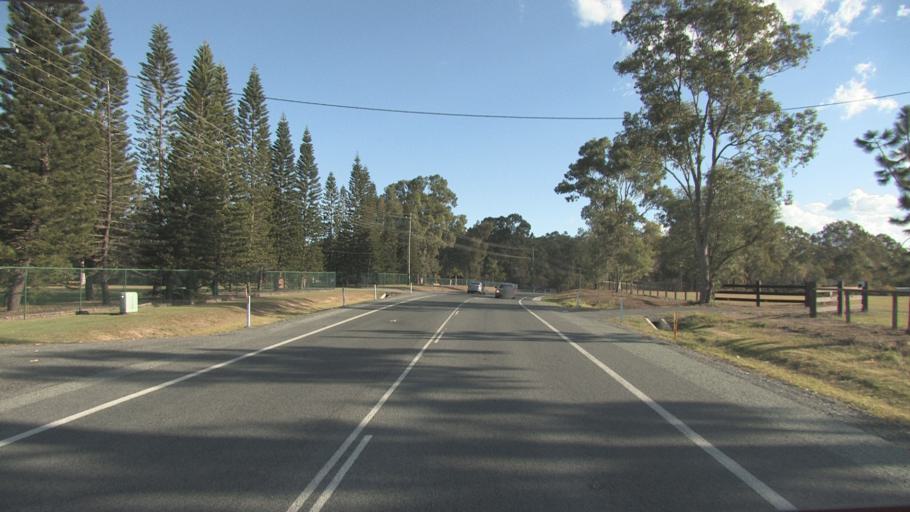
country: AU
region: Queensland
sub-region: Logan
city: Park Ridge South
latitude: -27.7192
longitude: 152.9688
